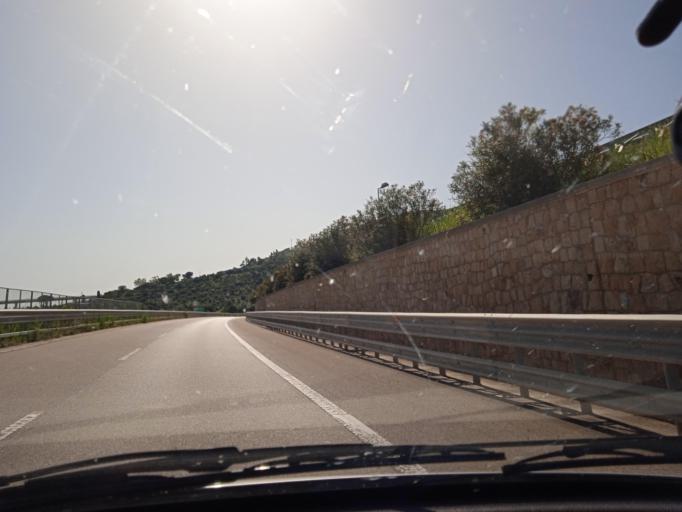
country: IT
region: Sicily
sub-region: Messina
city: Santo Stefano di Camastra
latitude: 38.0063
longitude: 14.3234
